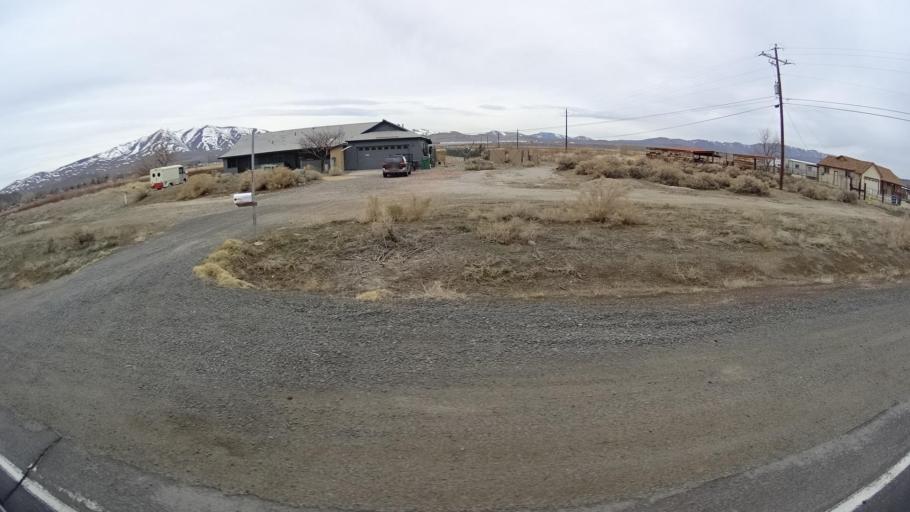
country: US
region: Nevada
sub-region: Washoe County
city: Lemmon Valley
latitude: 39.6503
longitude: -119.8285
